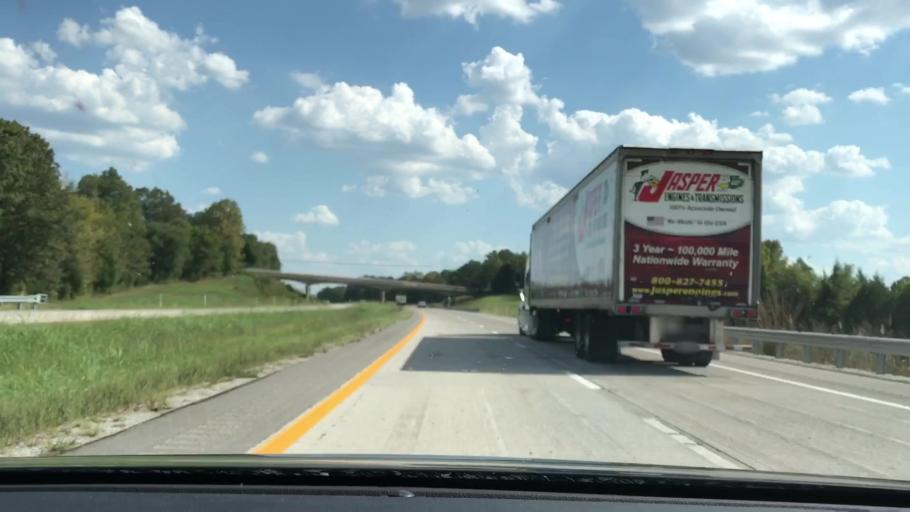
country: US
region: Kentucky
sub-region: Ohio County
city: Oak Grove
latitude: 37.3525
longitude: -86.7867
